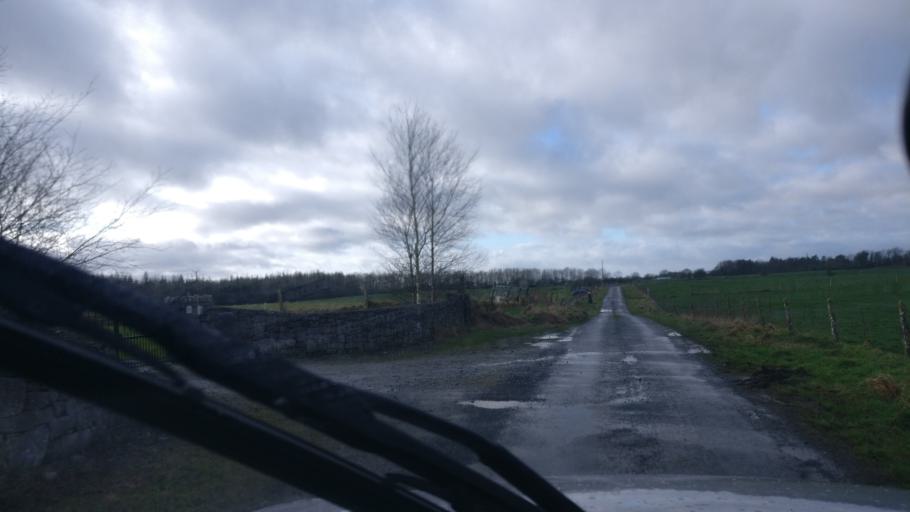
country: IE
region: Connaught
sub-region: County Galway
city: Loughrea
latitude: 53.2416
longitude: -8.6469
